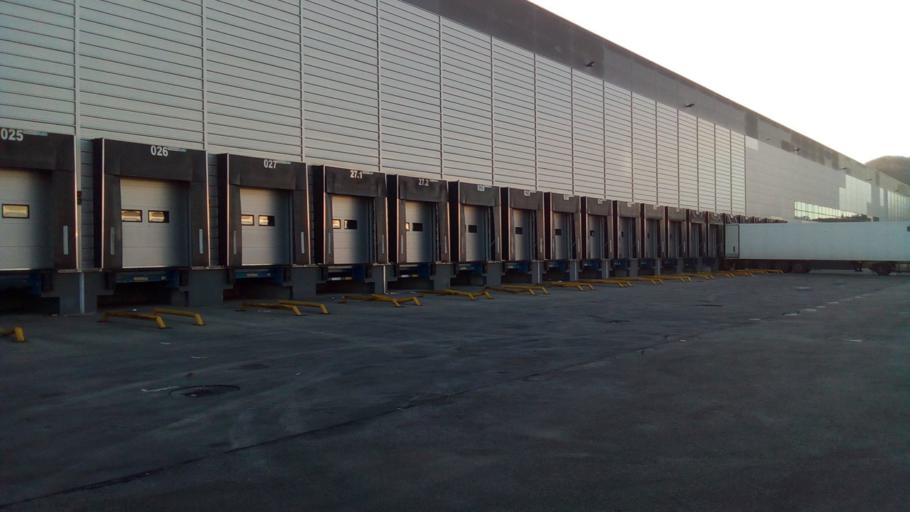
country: HR
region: Zagrebacka
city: Bestovje
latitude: 45.8050
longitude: 15.7720
